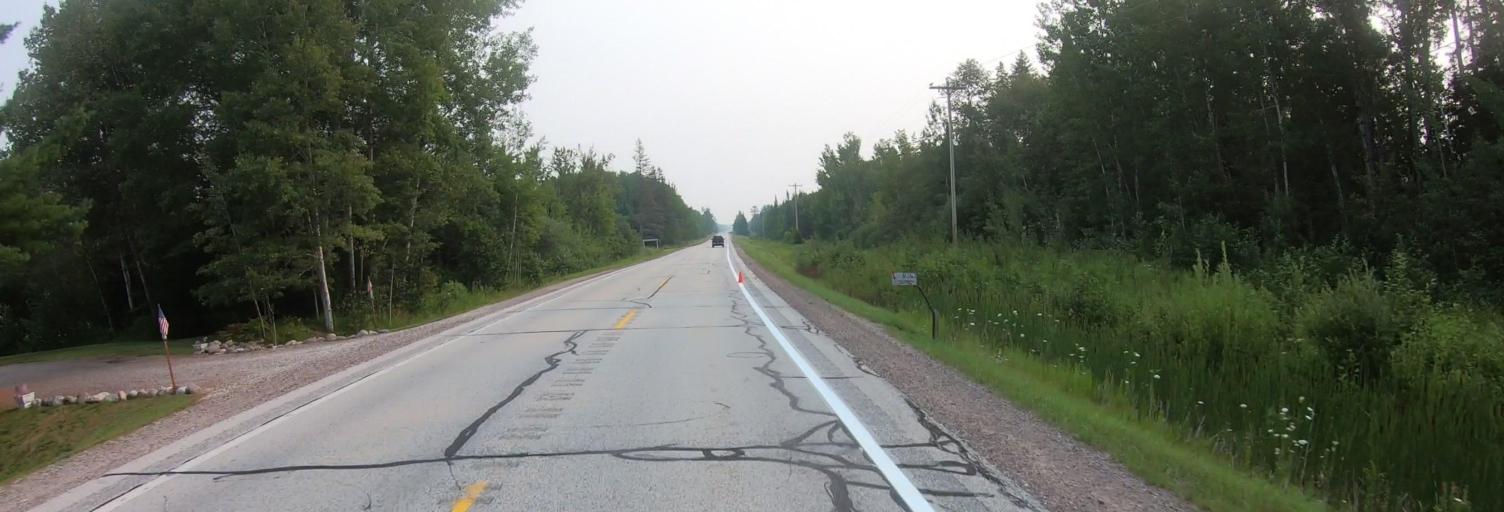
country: US
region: Michigan
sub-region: Luce County
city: Newberry
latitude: 46.5114
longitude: -85.0895
